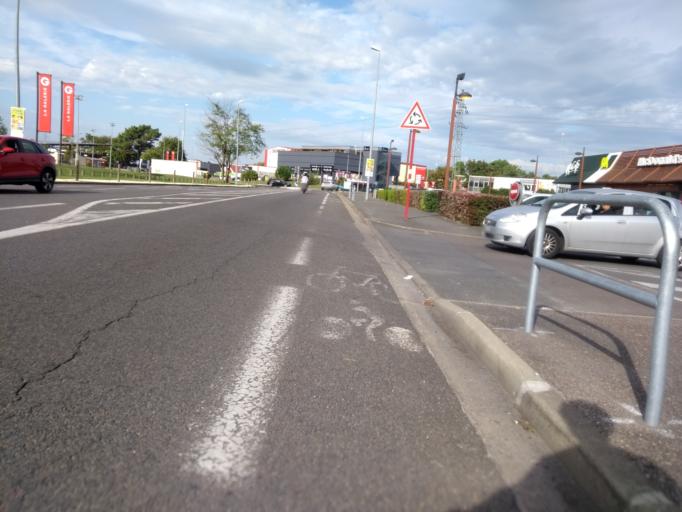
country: FR
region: Aquitaine
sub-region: Departement de la Gironde
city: Canejan
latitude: 44.7859
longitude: -0.6363
